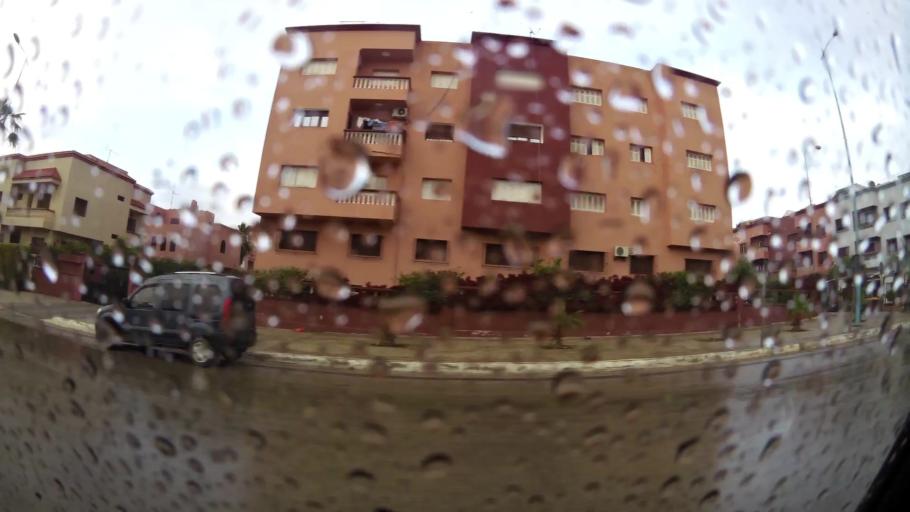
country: MA
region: Doukkala-Abda
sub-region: El-Jadida
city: El Jadida
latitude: 33.2383
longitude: -8.5280
